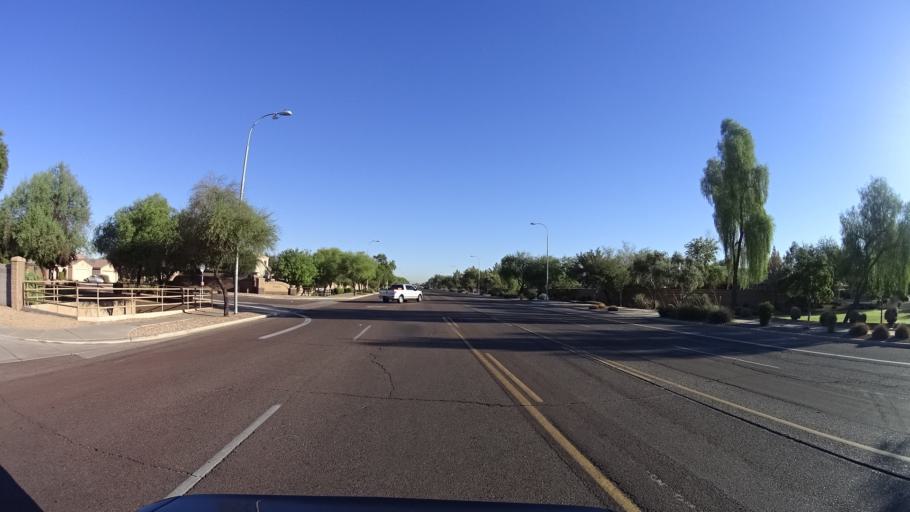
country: US
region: Arizona
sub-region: Maricopa County
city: Tolleson
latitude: 33.4252
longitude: -112.2386
